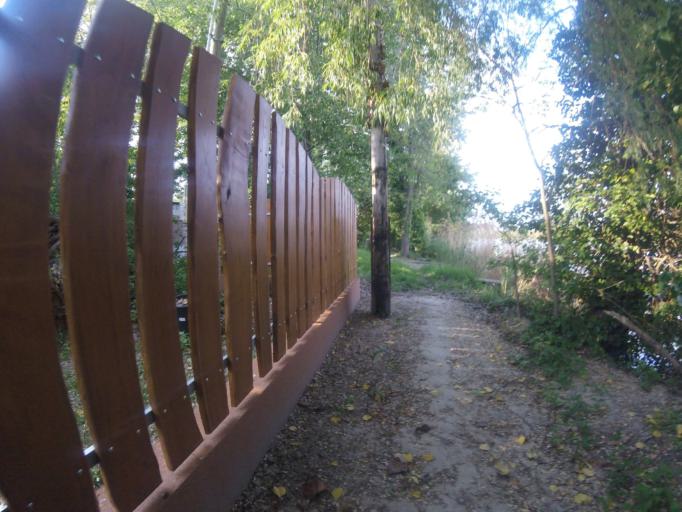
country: HU
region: Pest
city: Rackeve
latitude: 47.1901
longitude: 18.9547
